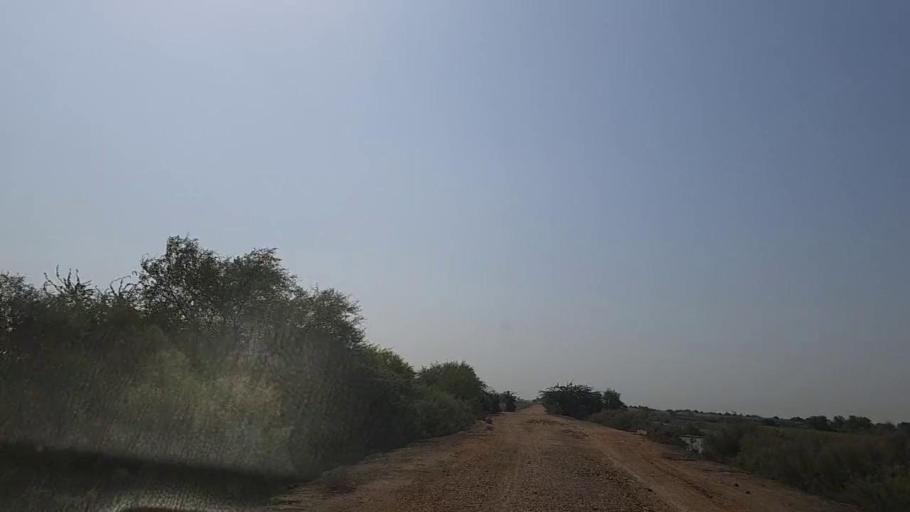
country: PK
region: Sindh
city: Daro Mehar
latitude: 24.6997
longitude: 68.1276
